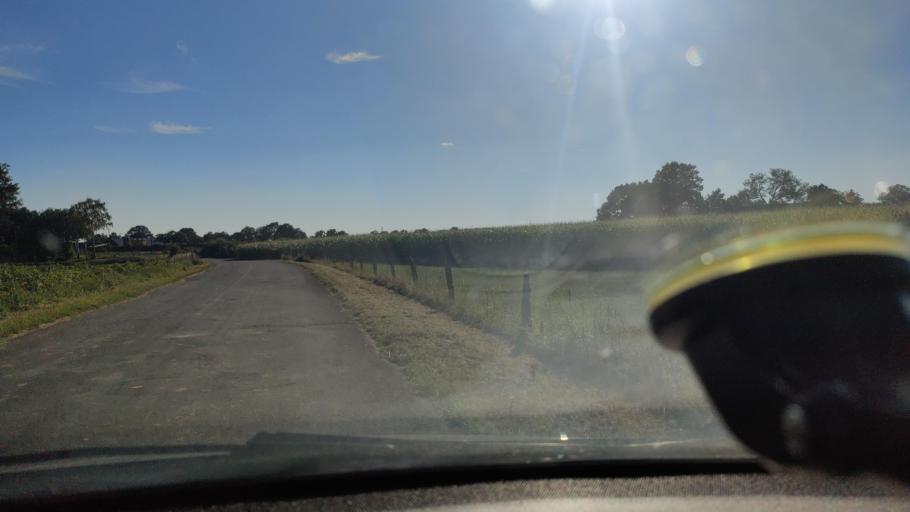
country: DE
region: North Rhine-Westphalia
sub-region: Regierungsbezirk Dusseldorf
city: Goch
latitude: 51.6624
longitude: 6.1049
